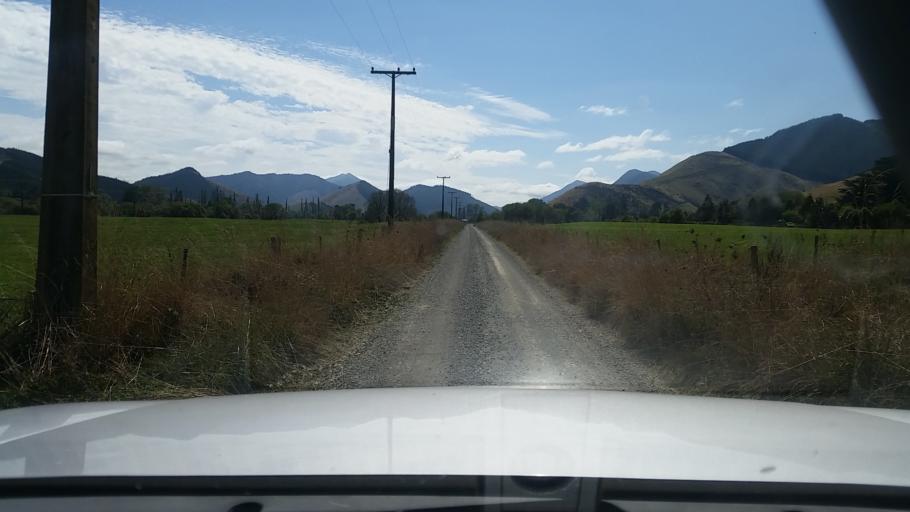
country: NZ
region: Nelson
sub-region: Nelson City
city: Nelson
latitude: -41.2590
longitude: 173.5816
